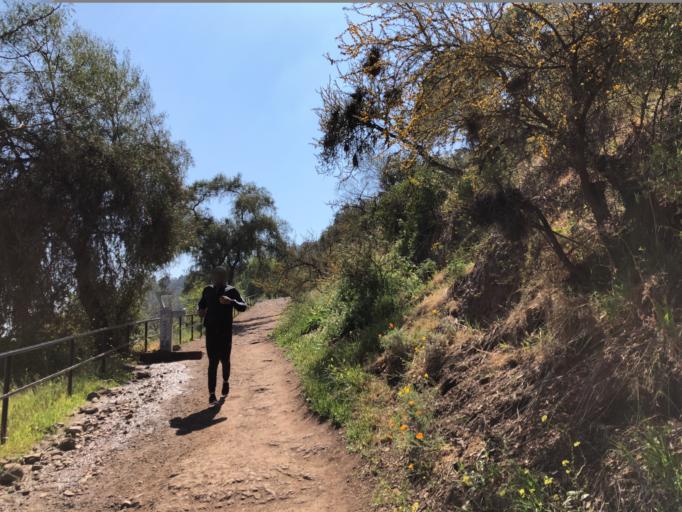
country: CL
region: Santiago Metropolitan
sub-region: Provincia de Santiago
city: Santiago
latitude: -33.4261
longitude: -70.6374
